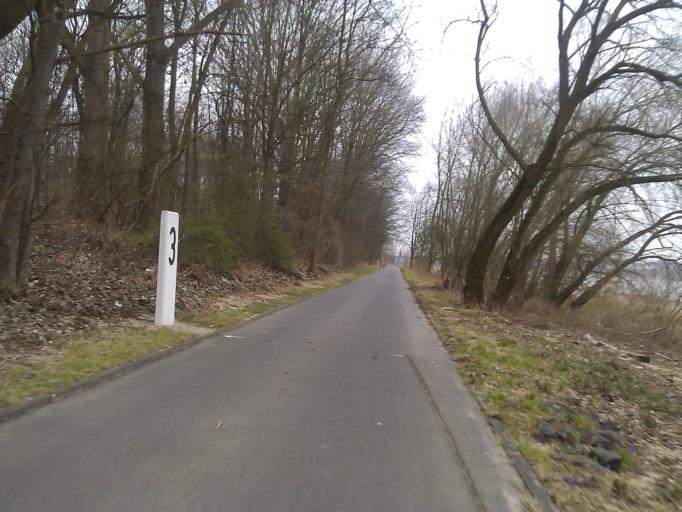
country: DE
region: North Rhine-Westphalia
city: Niederkassel
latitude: 50.8210
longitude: 7.0150
